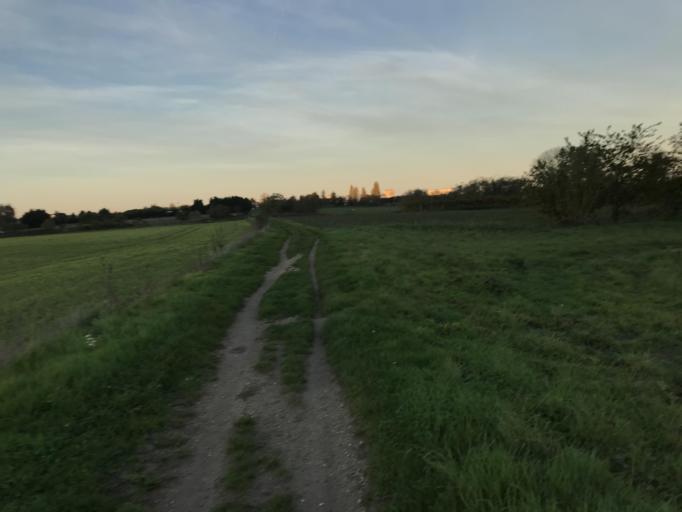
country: FR
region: Ile-de-France
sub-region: Departement de l'Essonne
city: Saulx-les-Chartreux
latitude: 48.6786
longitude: 2.2795
